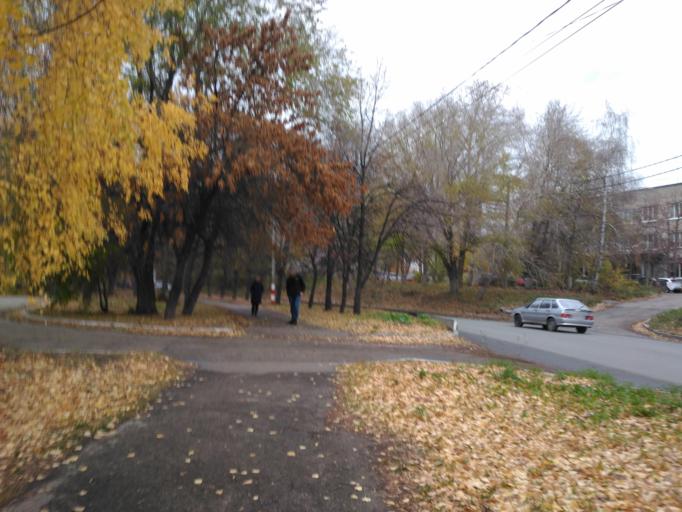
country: RU
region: Ulyanovsk
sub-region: Ulyanovskiy Rayon
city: Ulyanovsk
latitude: 54.3392
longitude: 48.3943
